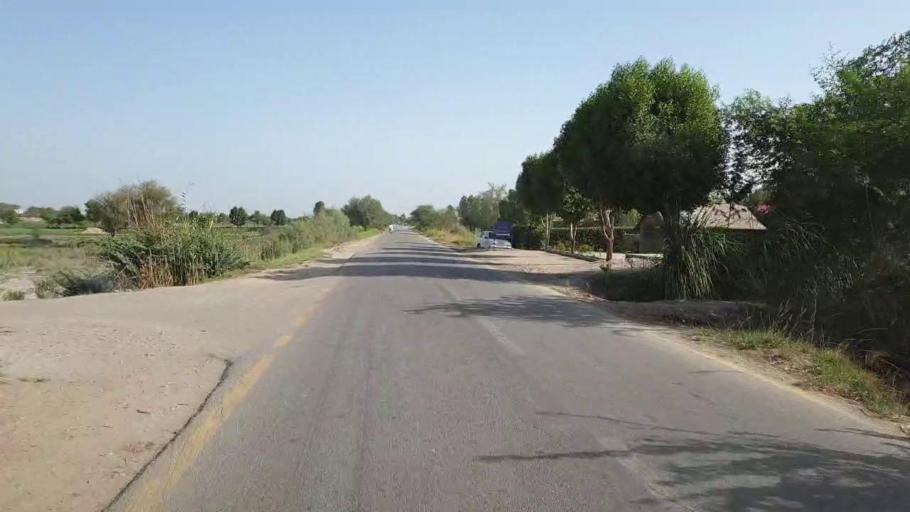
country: PK
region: Sindh
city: Daur
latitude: 26.4548
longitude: 68.4506
